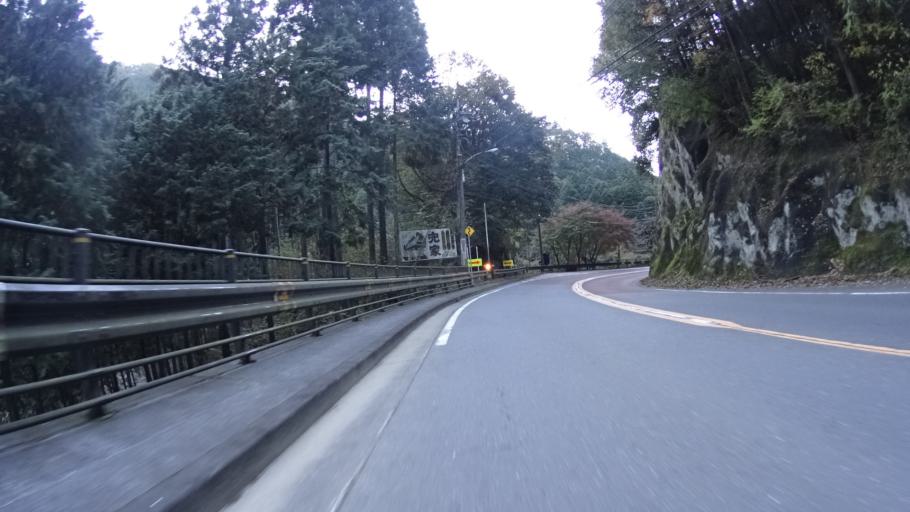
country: JP
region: Tokyo
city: Itsukaichi
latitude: 35.7201
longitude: 139.1507
